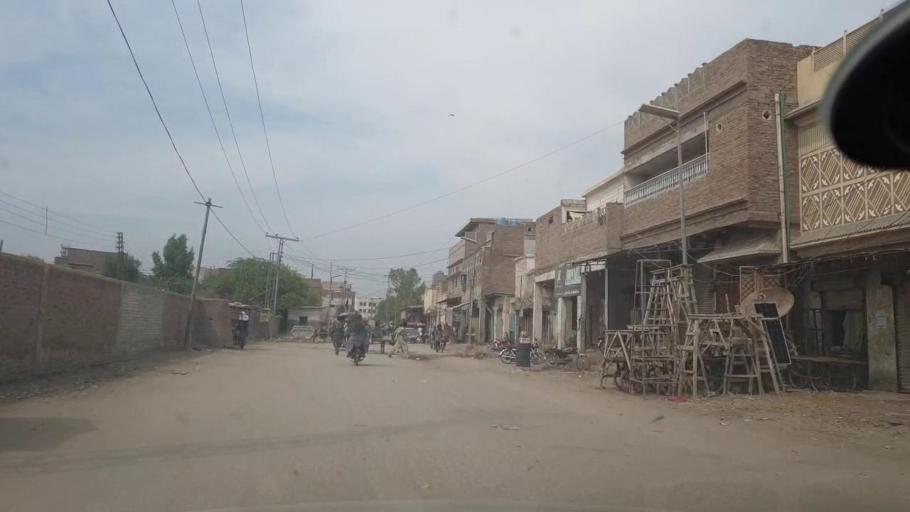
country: PK
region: Sindh
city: Jacobabad
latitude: 28.2763
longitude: 68.4381
